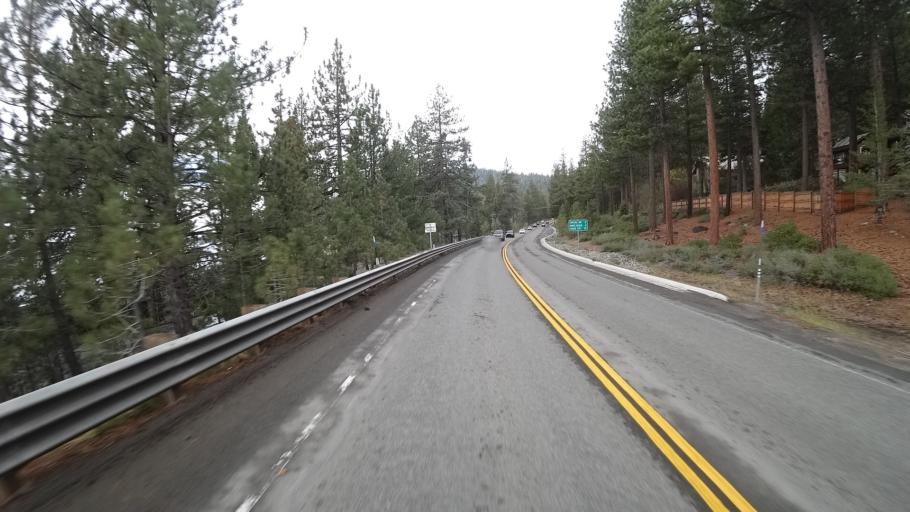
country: US
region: Nevada
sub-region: Washoe County
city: Incline Village
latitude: 39.2495
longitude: -119.9835
